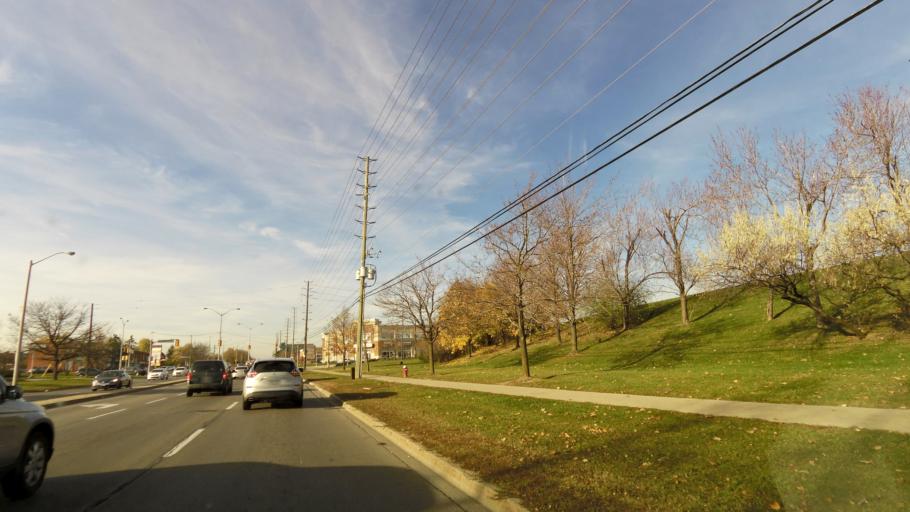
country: CA
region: Ontario
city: Brampton
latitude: 43.7484
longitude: -79.7257
